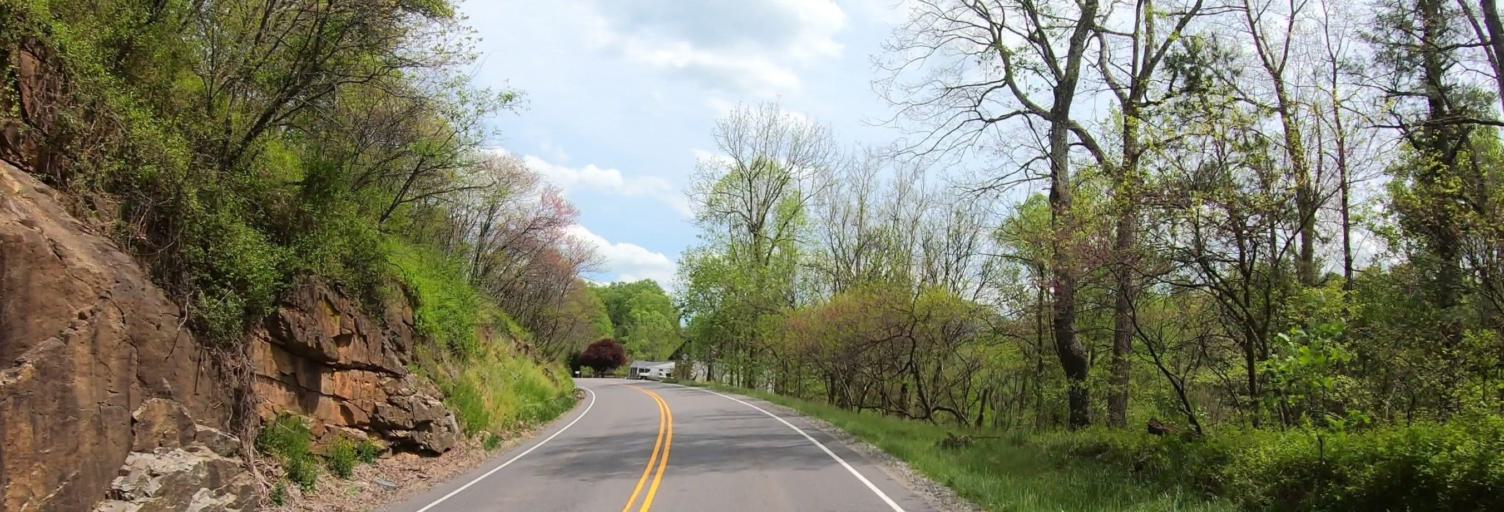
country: US
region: Virginia
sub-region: Roanoke County
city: Cave Spring
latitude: 37.1993
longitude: -80.0658
